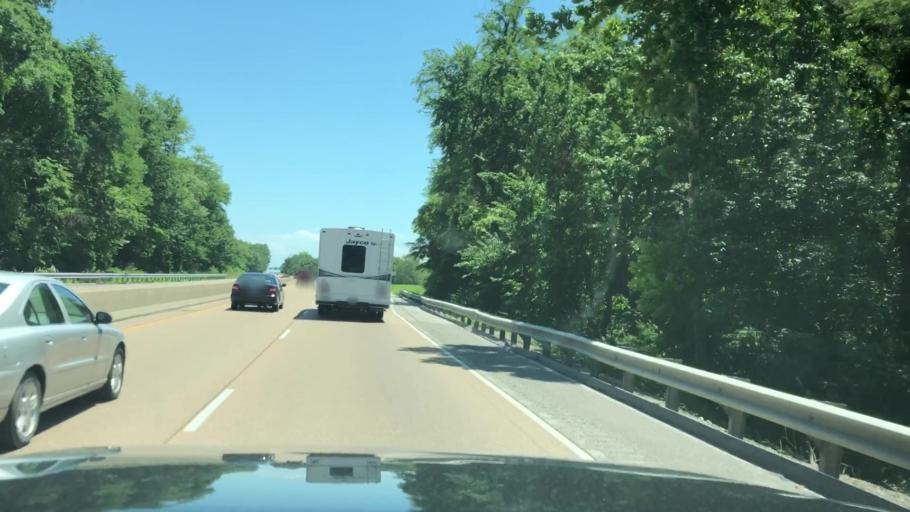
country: US
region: Illinois
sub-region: Saint Clair County
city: Alorton
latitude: 38.5573
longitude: -90.0802
